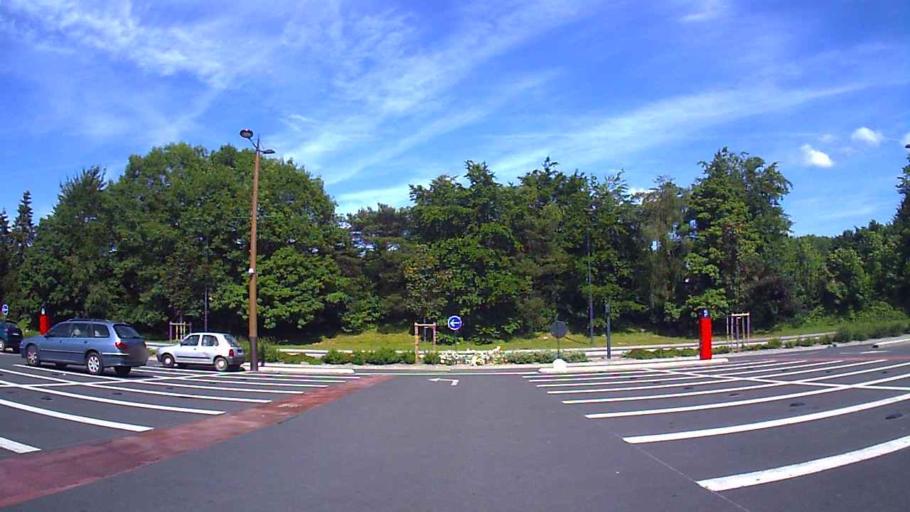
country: FR
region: Brittany
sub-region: Departement d'Ille-et-Vilaine
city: Rennes
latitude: 48.0826
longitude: -1.6759
